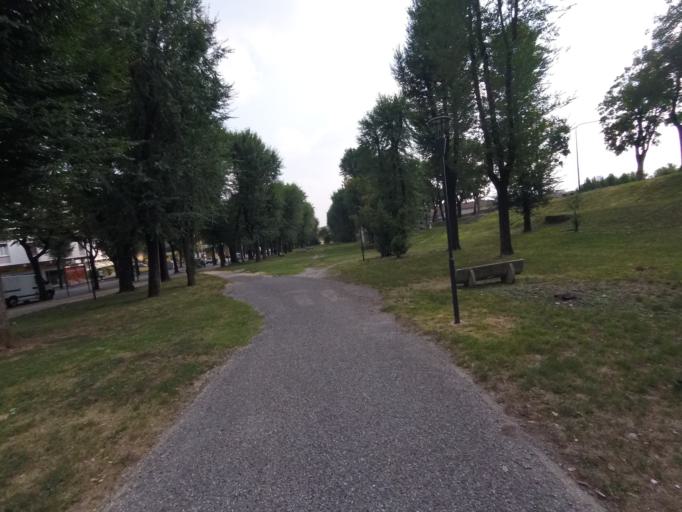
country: IT
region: Lombardy
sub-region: Provincia di Brescia
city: Brescia
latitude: 45.5407
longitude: 10.2312
